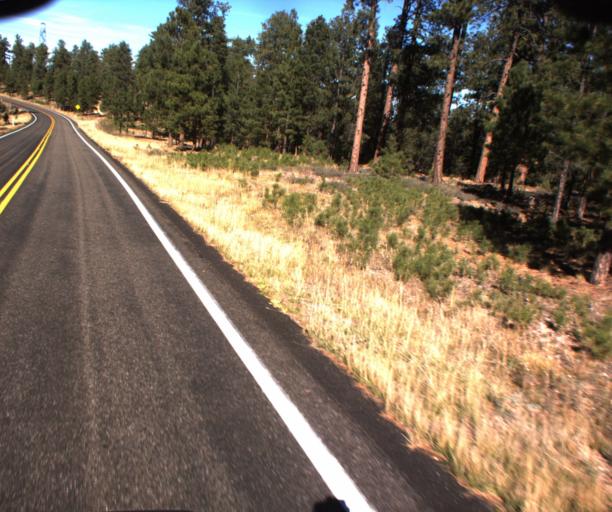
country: US
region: Arizona
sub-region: Coconino County
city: Fredonia
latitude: 36.6965
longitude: -112.2137
